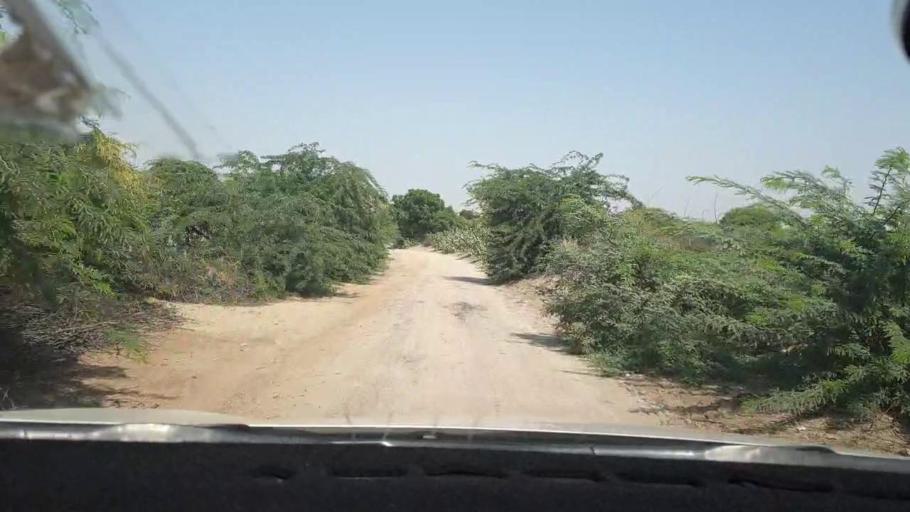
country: PK
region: Sindh
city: Tando Mittha Khan
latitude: 25.8797
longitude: 69.3887
